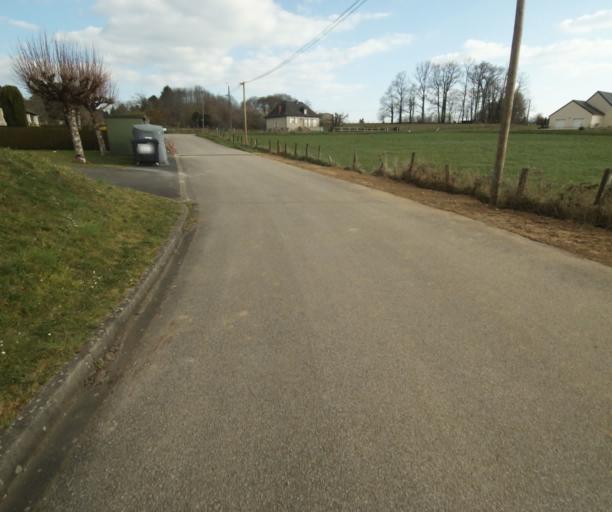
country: FR
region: Limousin
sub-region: Departement de la Correze
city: Saint-Clement
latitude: 45.3509
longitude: 1.6337
